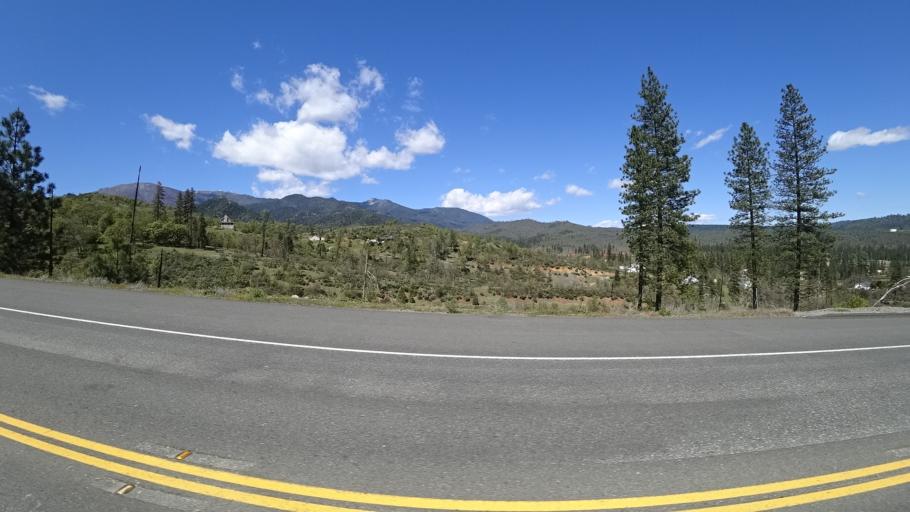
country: US
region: California
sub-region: Trinity County
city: Weaverville
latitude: 40.7352
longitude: -122.9593
